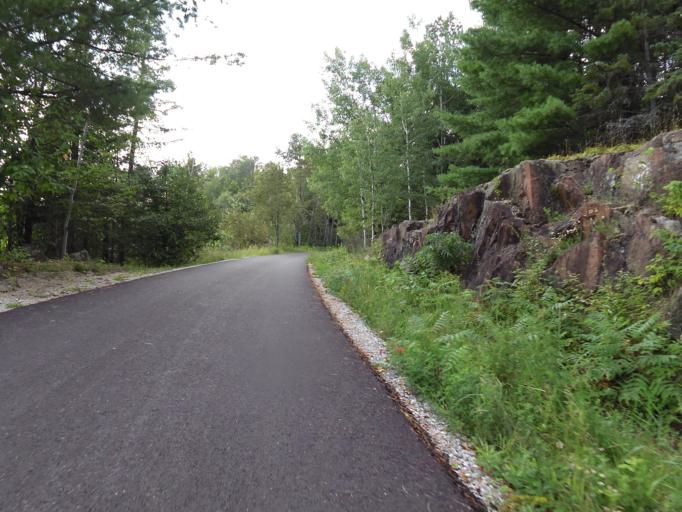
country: CA
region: Quebec
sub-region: Outaouais
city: Maniwaki
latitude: 46.1932
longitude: -76.0478
